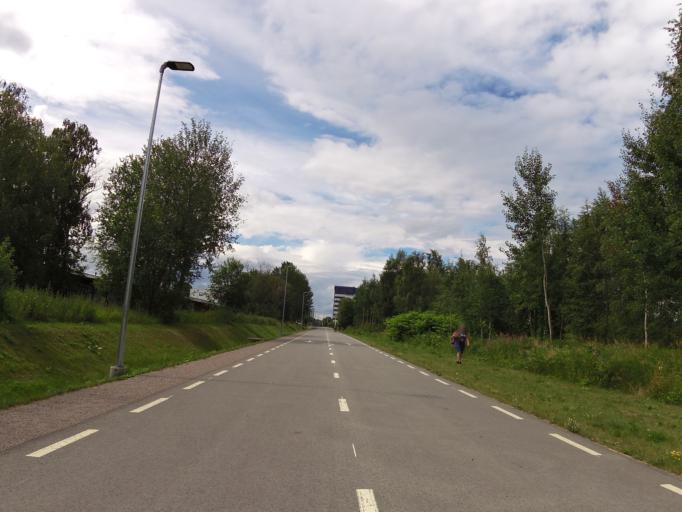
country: EE
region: Harju
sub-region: Saue vald
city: Laagri
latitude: 59.4152
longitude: 24.6665
